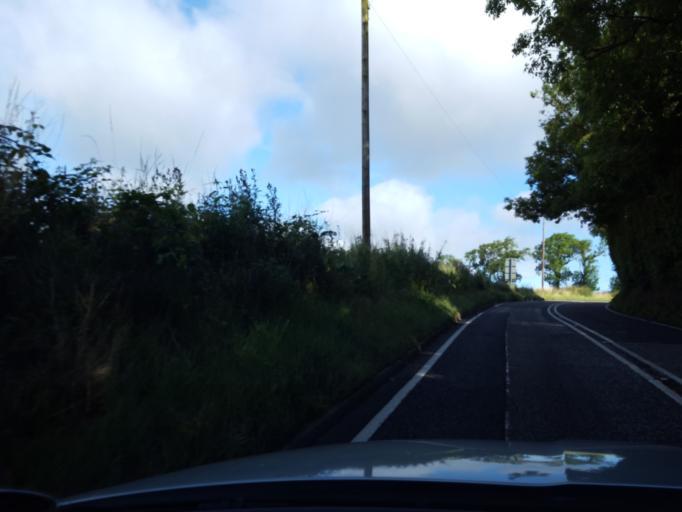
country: GB
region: Scotland
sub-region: West Lothian
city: Broxburn
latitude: 55.9486
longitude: -3.5091
